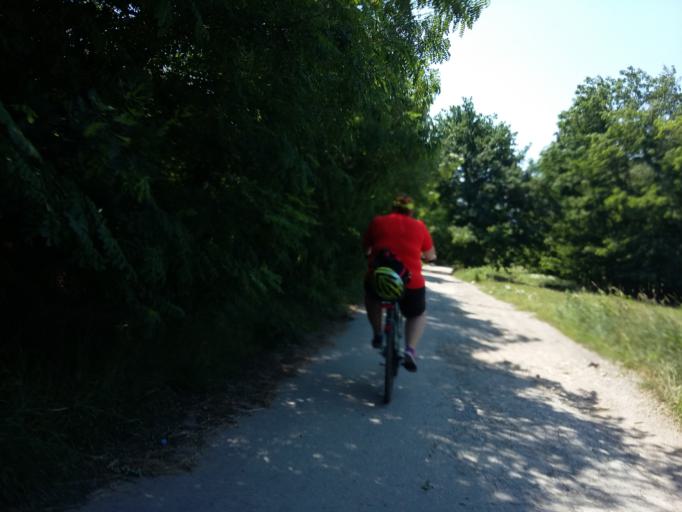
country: AT
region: Lower Austria
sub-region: Politischer Bezirk Ganserndorf
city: Marchegg
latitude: 48.2763
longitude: 16.9659
